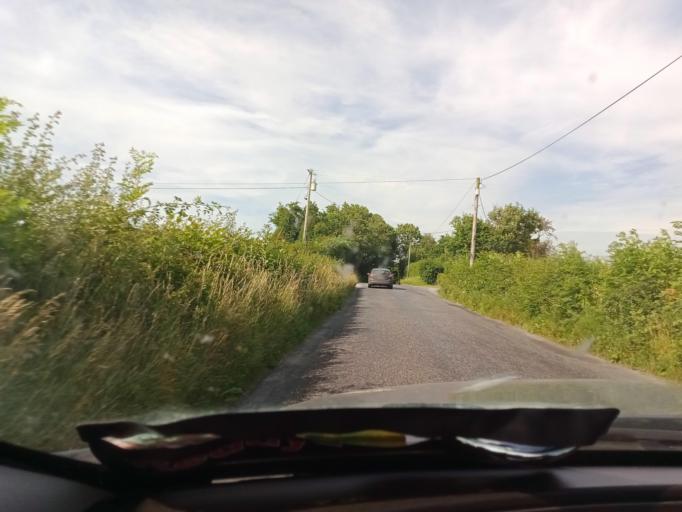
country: IE
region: Leinster
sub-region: Laois
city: Mountmellick
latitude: 53.1428
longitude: -7.3702
